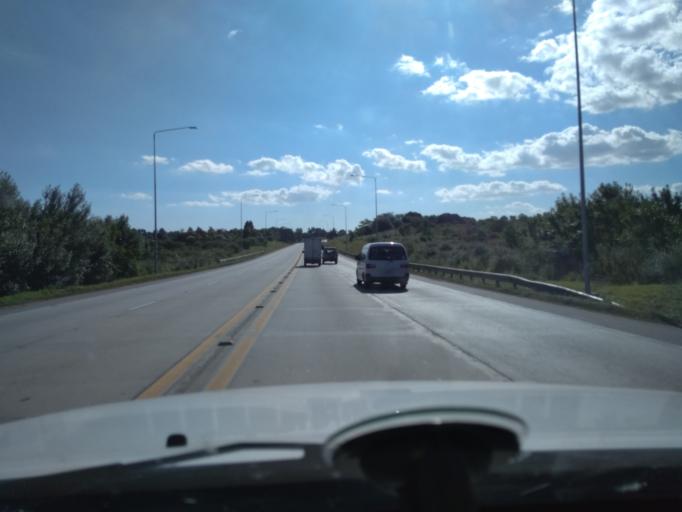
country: UY
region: Canelones
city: La Paz
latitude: -34.7815
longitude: -56.2415
